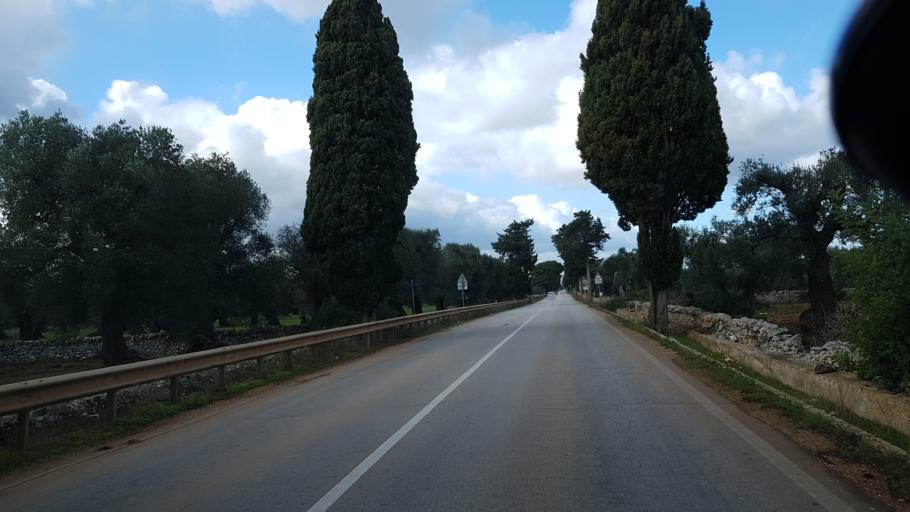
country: IT
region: Apulia
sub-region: Provincia di Brindisi
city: Montalbano
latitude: 40.7673
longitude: 17.5136
